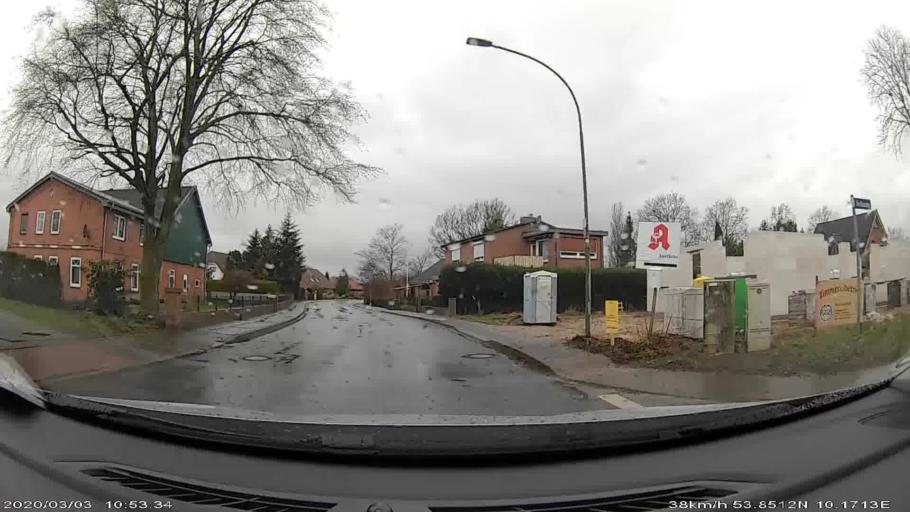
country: DE
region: Schleswig-Holstein
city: Seth
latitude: 53.8518
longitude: 10.1683
